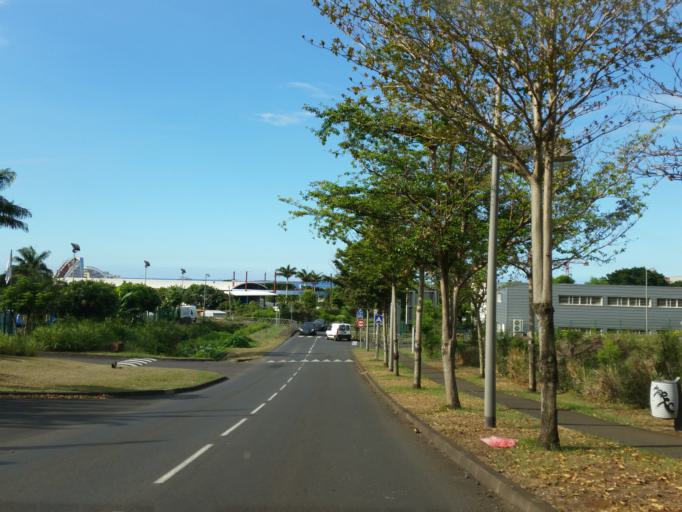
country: RE
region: Reunion
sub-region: Reunion
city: Sainte-Marie
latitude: -20.9046
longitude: 55.4983
